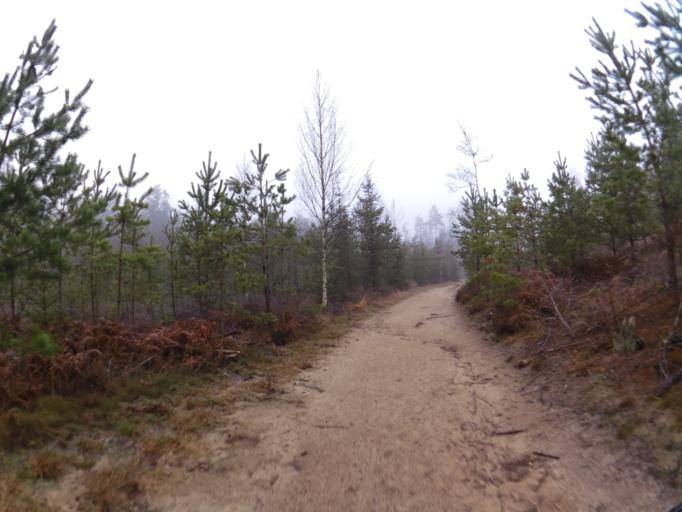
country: NO
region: Ostfold
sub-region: Fredrikstad
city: Fredrikstad
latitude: 59.2632
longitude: 10.9839
